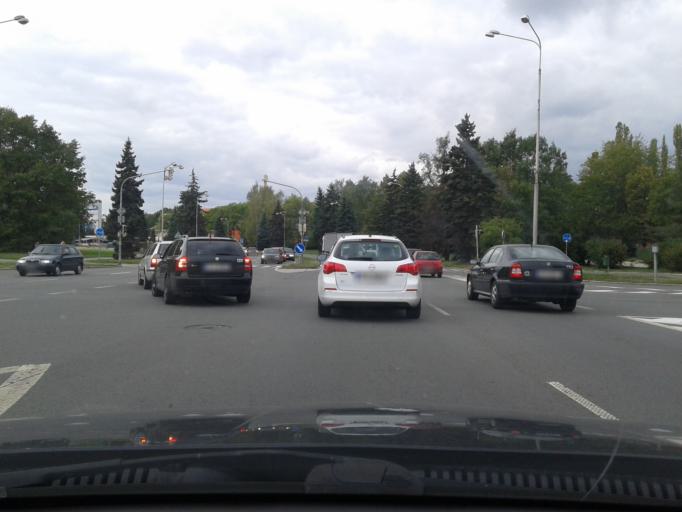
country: CZ
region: Moravskoslezsky
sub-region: Okres Karvina
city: Karvina
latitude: 49.8566
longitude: 18.5459
